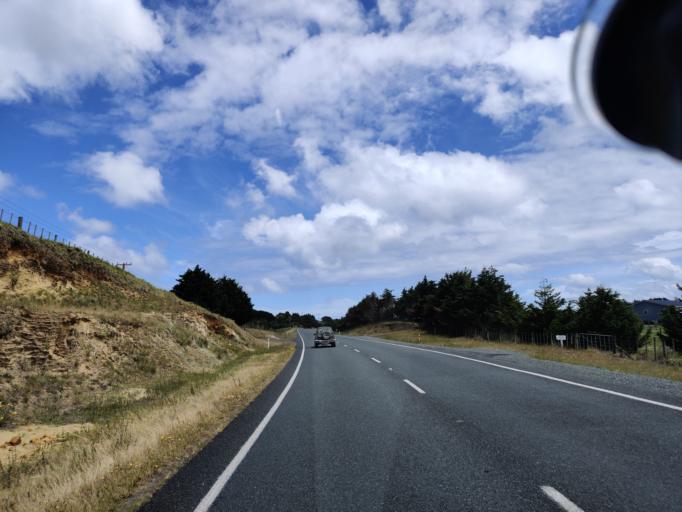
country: NZ
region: Northland
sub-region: Far North District
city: Kaitaia
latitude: -34.8974
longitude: 173.1728
